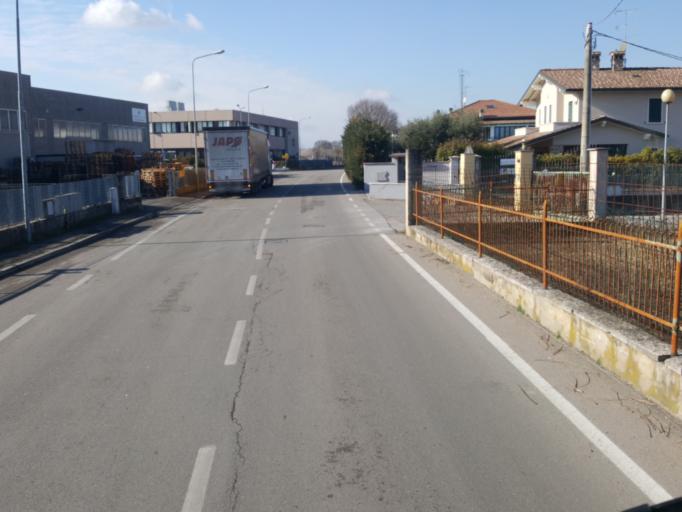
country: IT
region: Veneto
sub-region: Provincia di Verona
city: Castelnuovo del Garda
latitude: 45.4295
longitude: 10.7566
